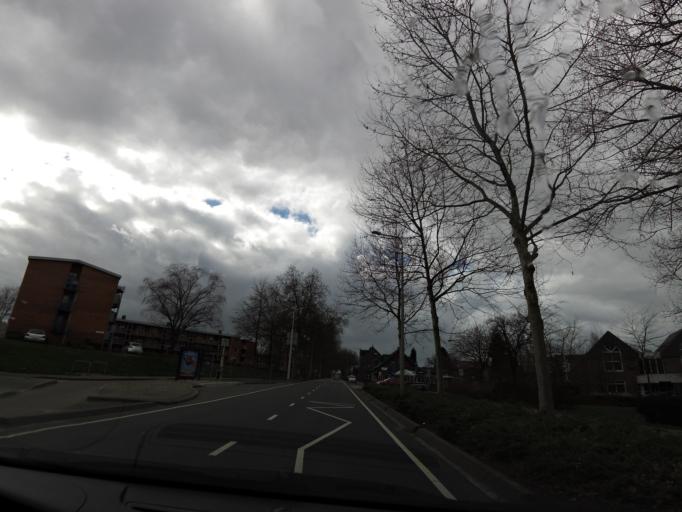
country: NL
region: Limburg
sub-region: Gemeente Venlo
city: Tegelen
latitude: 51.3365
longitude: 6.1304
